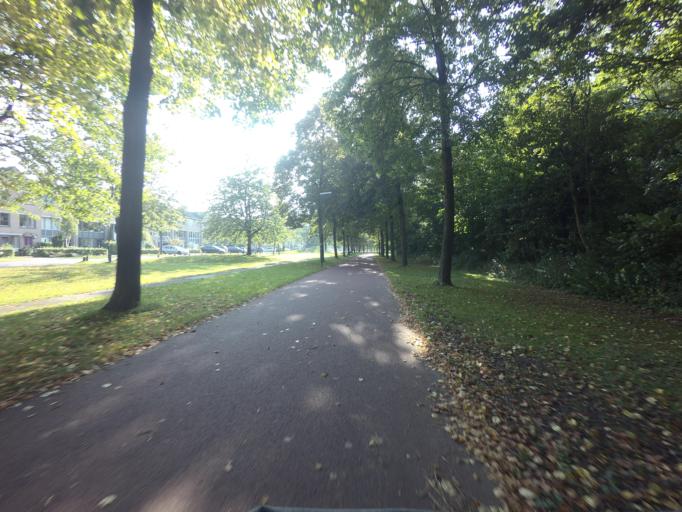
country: NL
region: Utrecht
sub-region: Gemeente Houten
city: Houten
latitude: 52.0387
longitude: 5.1808
